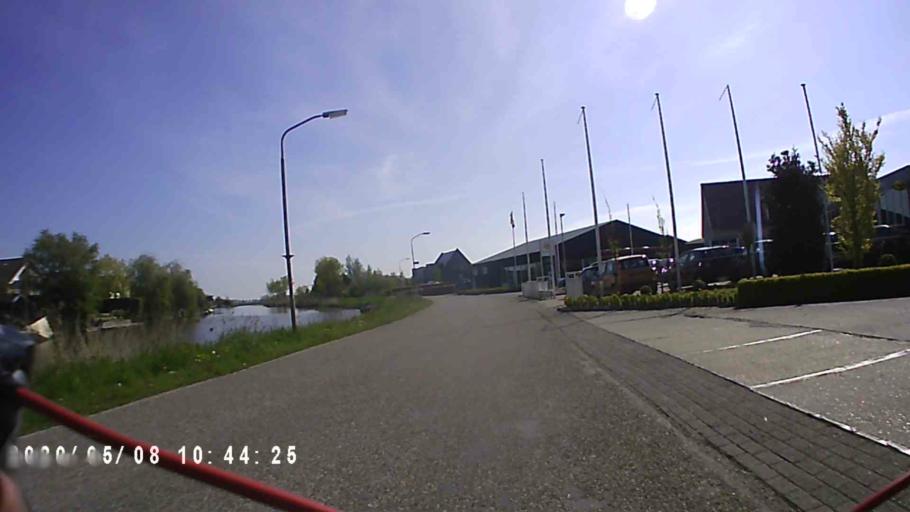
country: NL
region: Groningen
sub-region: Gemeente Winsum
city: Winsum
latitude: 53.3328
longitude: 6.5277
